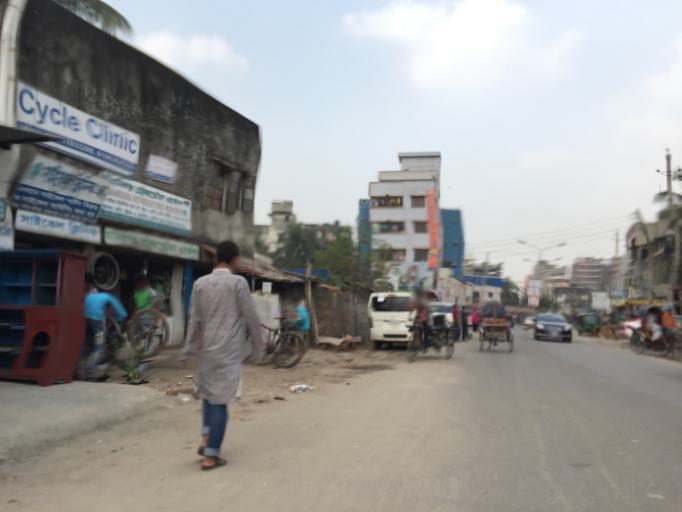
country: BD
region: Dhaka
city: Azimpur
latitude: 23.7949
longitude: 90.3653
